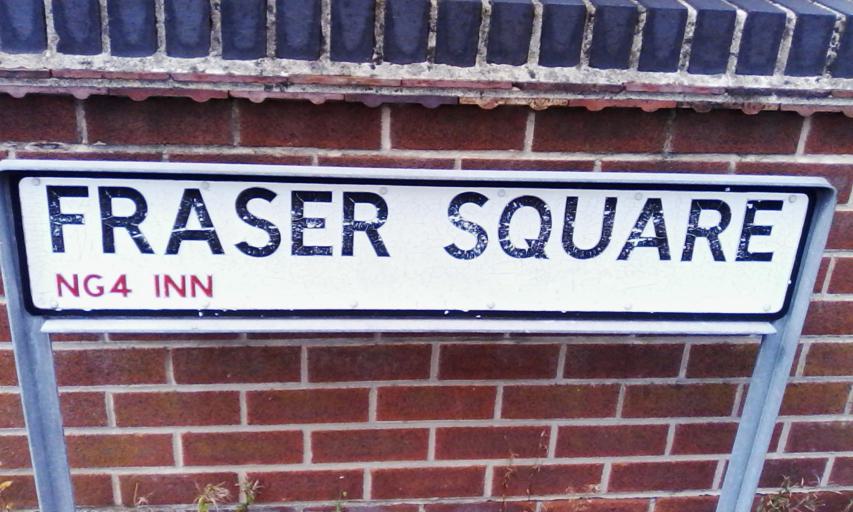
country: GB
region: England
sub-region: Nottinghamshire
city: Arnold
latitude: 52.9768
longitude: -1.1068
